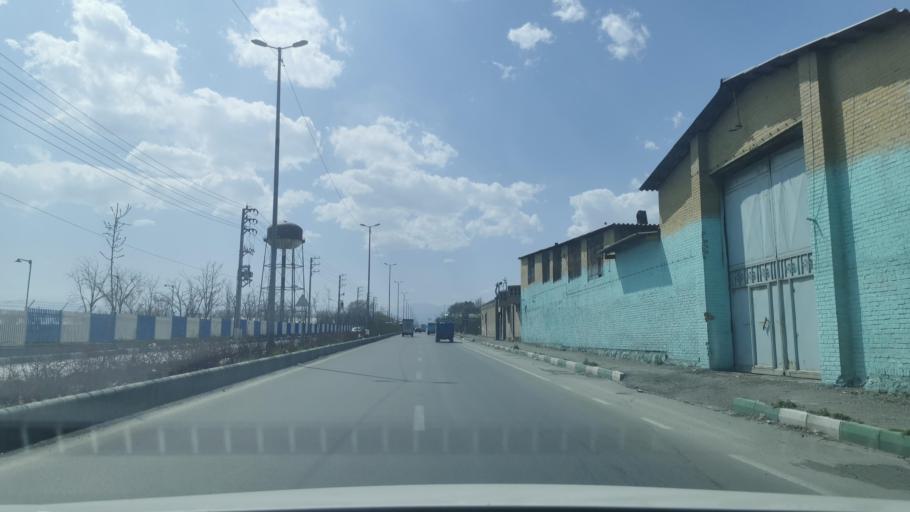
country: IR
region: Razavi Khorasan
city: Torqabeh
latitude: 36.4373
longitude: 59.4380
